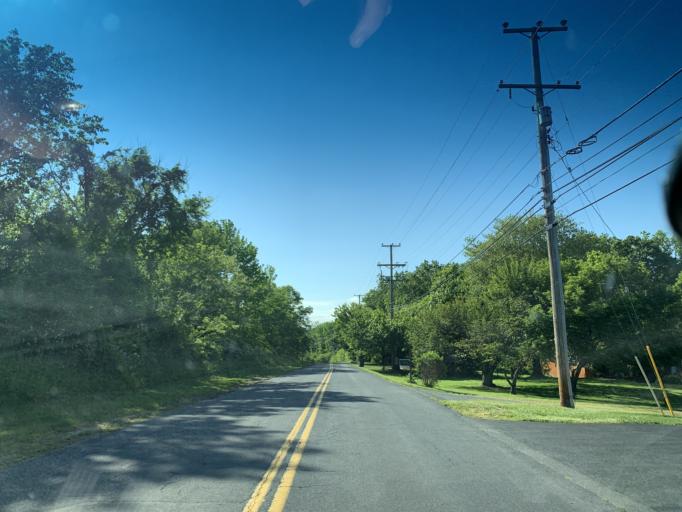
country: US
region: Maryland
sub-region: Harford County
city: Riverside
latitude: 39.4876
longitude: -76.2368
